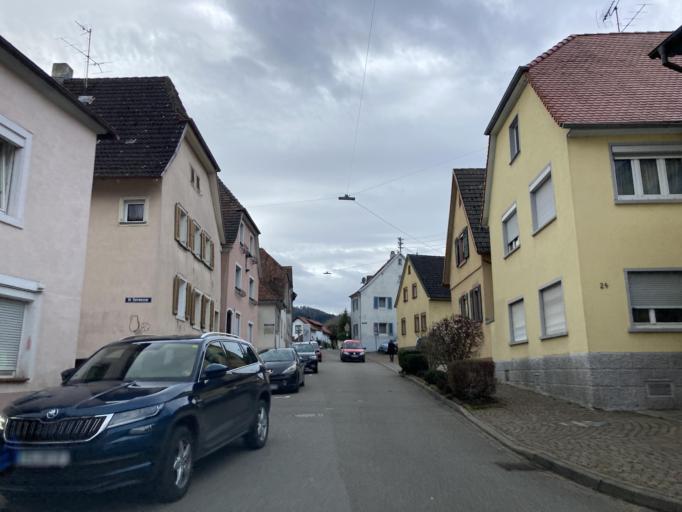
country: DE
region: Baden-Wuerttemberg
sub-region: Freiburg Region
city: Endingen
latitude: 48.1394
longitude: 7.7038
